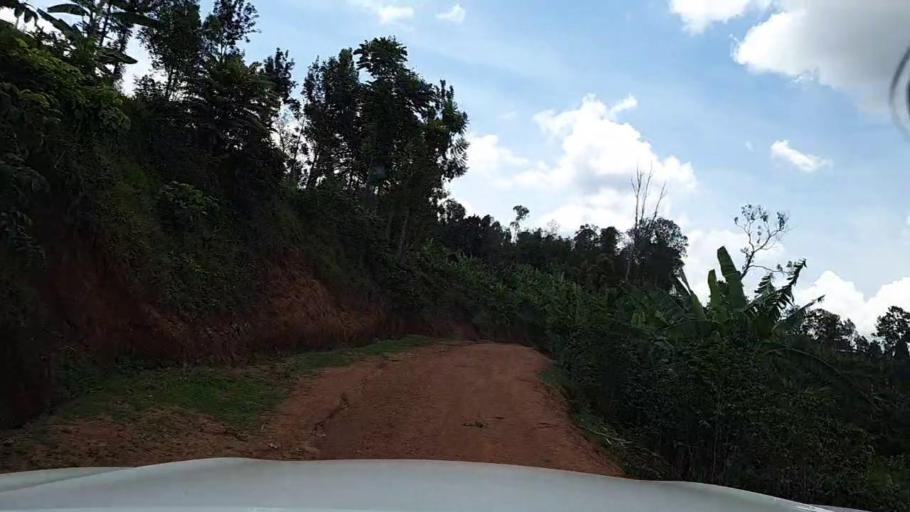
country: RW
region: Southern Province
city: Butare
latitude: -2.7522
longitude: 29.7610
